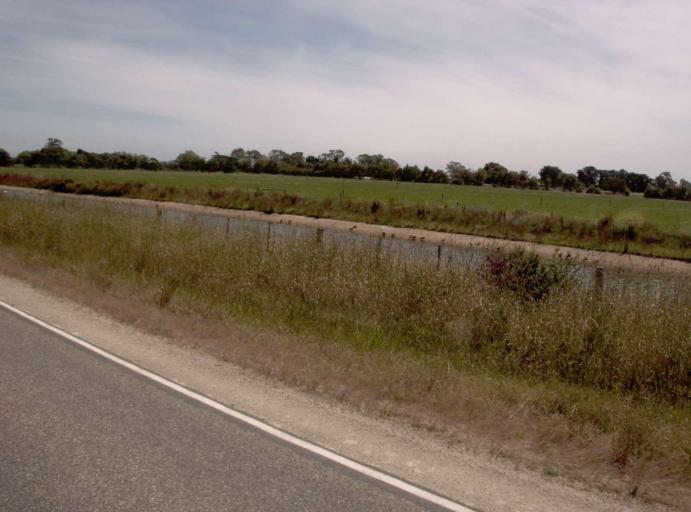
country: AU
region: Victoria
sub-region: Wellington
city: Heyfield
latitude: -38.0496
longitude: 146.8752
